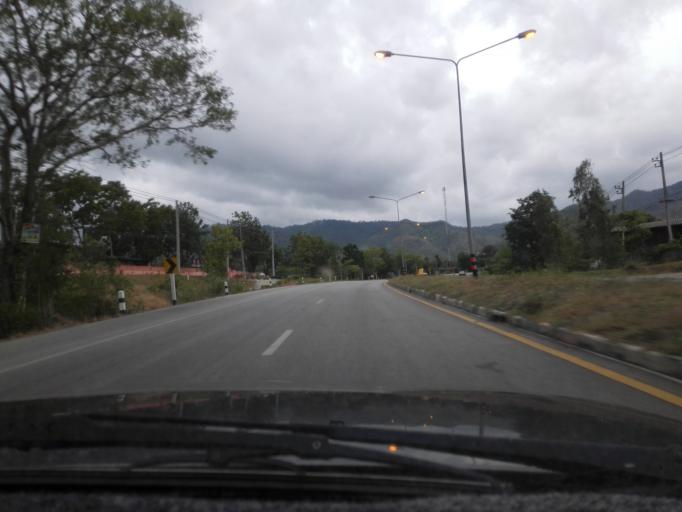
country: TH
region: Tak
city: Tak
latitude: 16.7943
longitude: 99.0295
